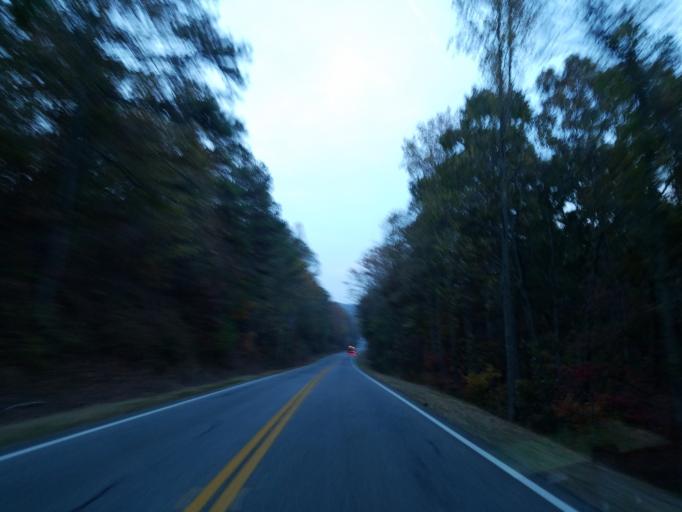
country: US
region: Georgia
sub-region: Pickens County
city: Jasper
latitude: 34.5383
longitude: -84.5777
